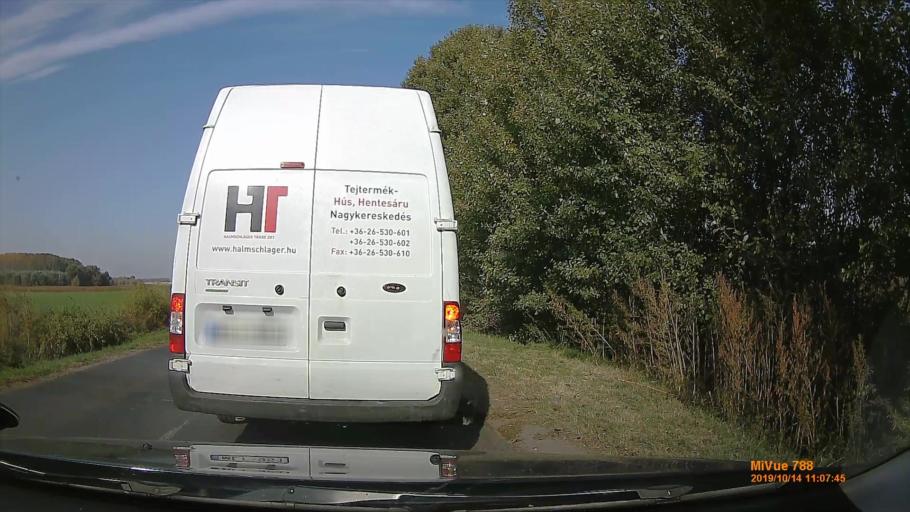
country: HU
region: Pest
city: Monor
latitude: 47.3673
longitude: 19.4252
